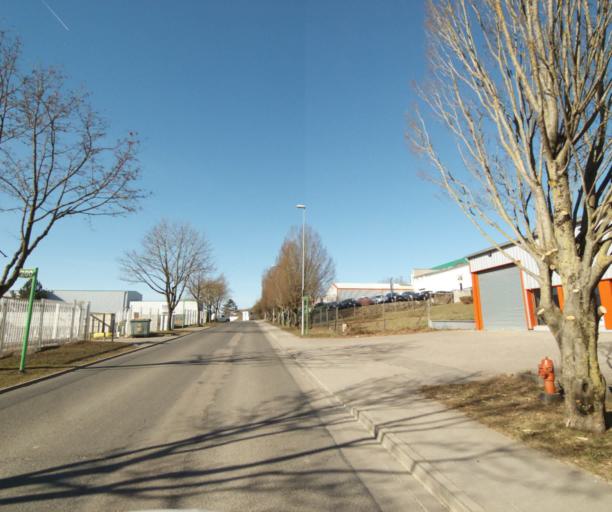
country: FR
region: Lorraine
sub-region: Departement de Meurthe-et-Moselle
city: Fleville-devant-Nancy
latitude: 48.6178
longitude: 6.1848
